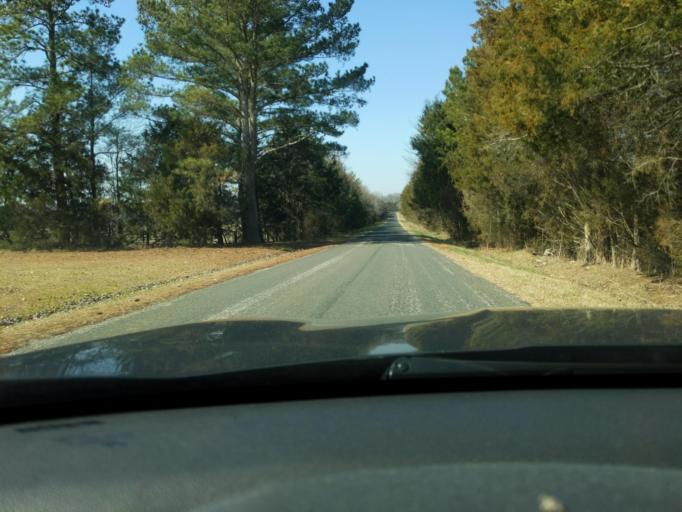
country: US
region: South Carolina
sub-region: Abbeville County
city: Calhoun Falls
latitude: 34.0854
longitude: -82.5459
